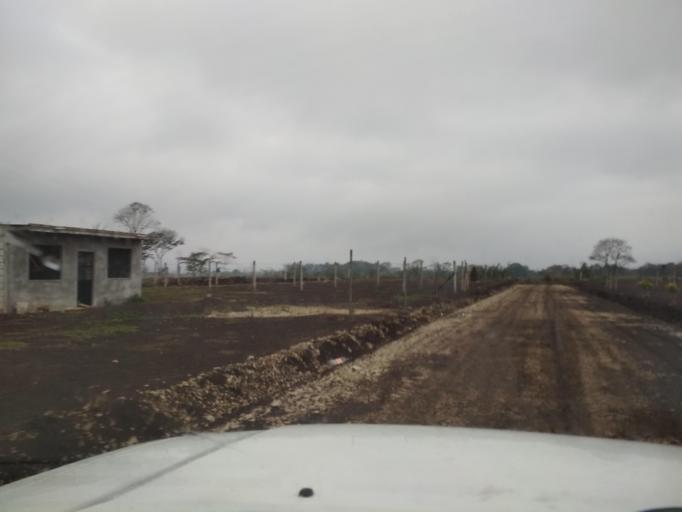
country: MX
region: Veracruz
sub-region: Cordoba
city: Veinte de Noviembre
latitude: 18.8585
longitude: -96.9623
